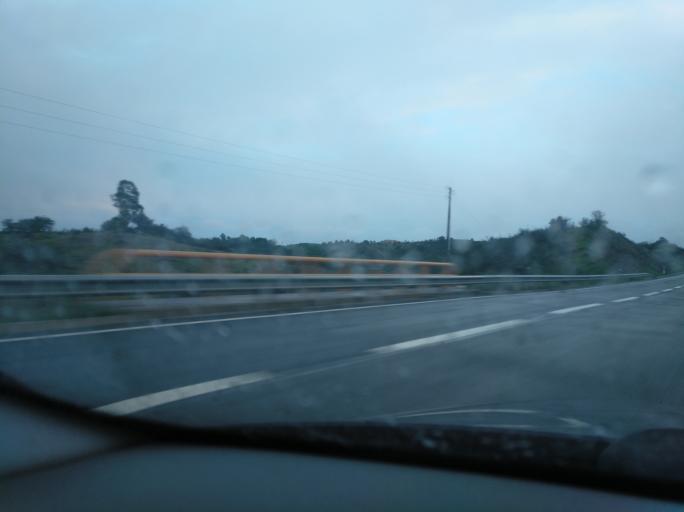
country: PT
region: Faro
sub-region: Castro Marim
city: Castro Marim
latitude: 37.2988
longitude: -7.4886
